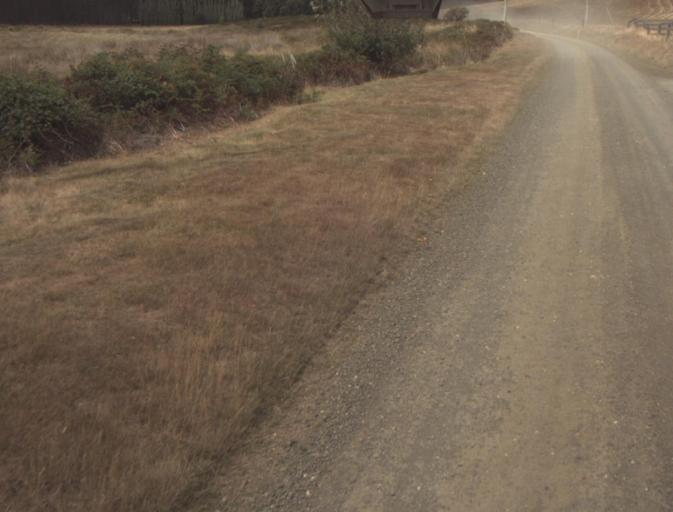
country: AU
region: Tasmania
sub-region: Dorset
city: Bridport
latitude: -41.1881
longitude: 147.2618
